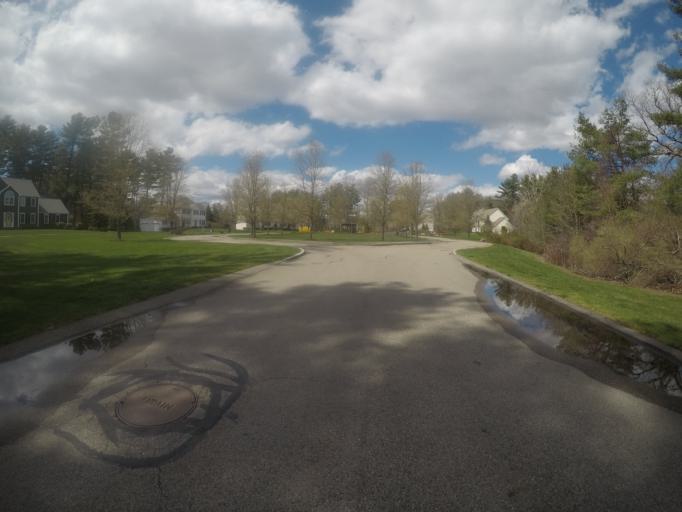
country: US
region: Massachusetts
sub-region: Bristol County
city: Easton
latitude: 42.0196
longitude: -71.0684
